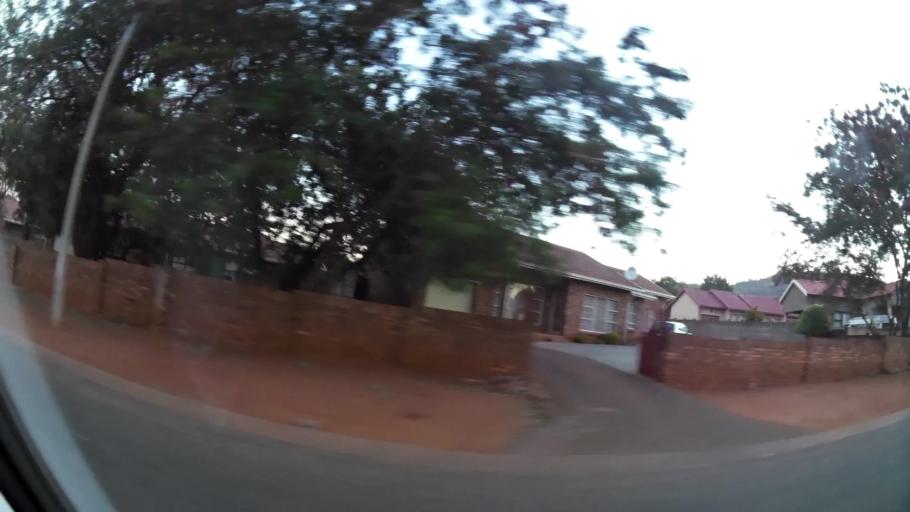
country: ZA
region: North-West
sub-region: Bojanala Platinum District Municipality
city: Rustenburg
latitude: -25.6603
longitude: 27.2082
